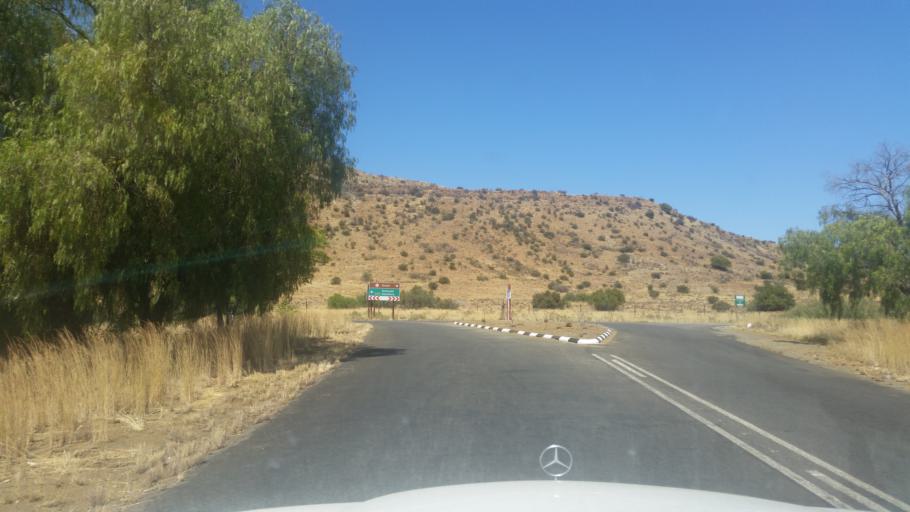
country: ZA
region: Eastern Cape
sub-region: Joe Gqabi District Municipality
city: Burgersdorp
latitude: -30.7435
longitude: 25.7569
